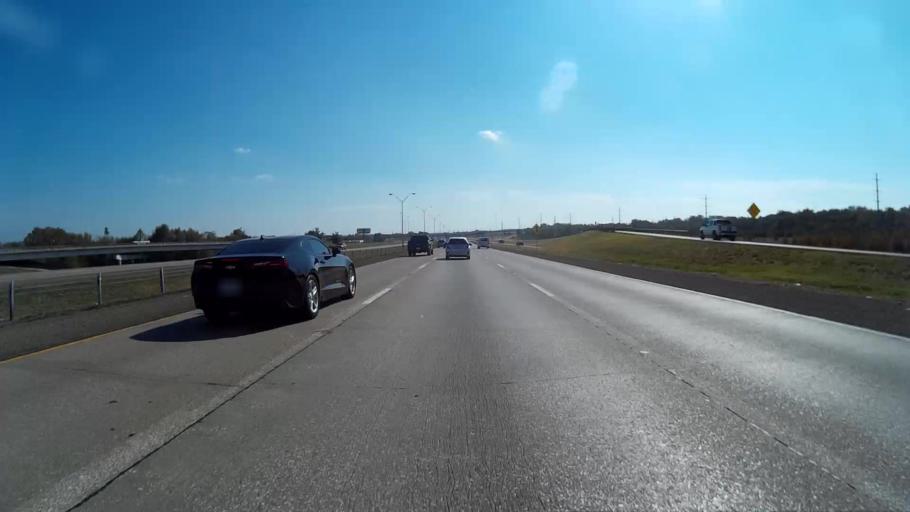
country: US
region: Texas
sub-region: Dallas County
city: Hutchins
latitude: 32.7105
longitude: -96.7559
